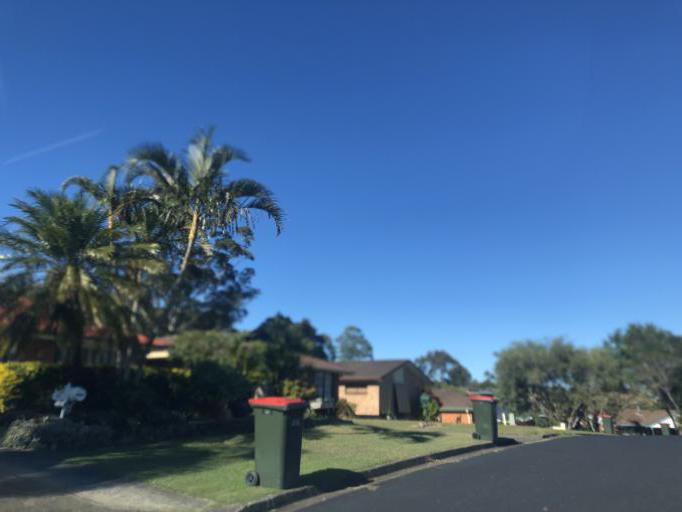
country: AU
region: New South Wales
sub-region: Coffs Harbour
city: Toormina
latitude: -30.3684
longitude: 153.0858
